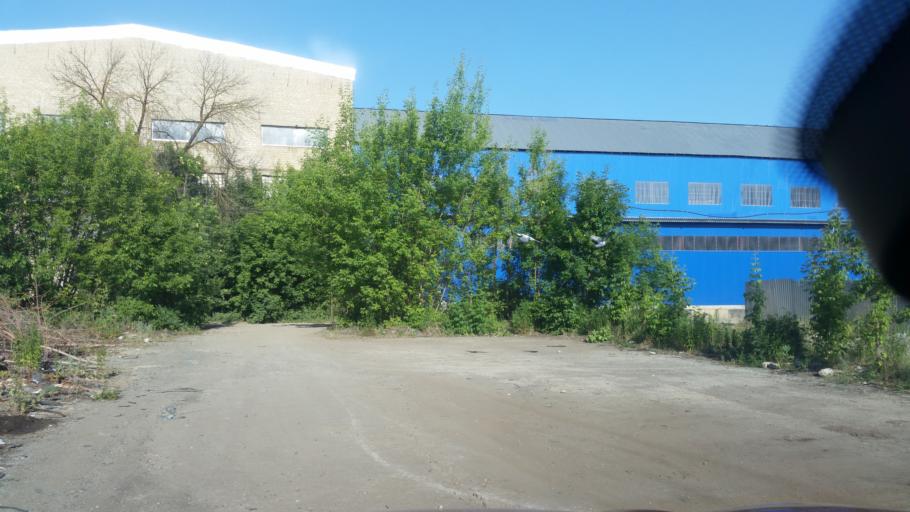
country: RU
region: Orjol
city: Znamenka
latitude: 52.9209
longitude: 35.9862
